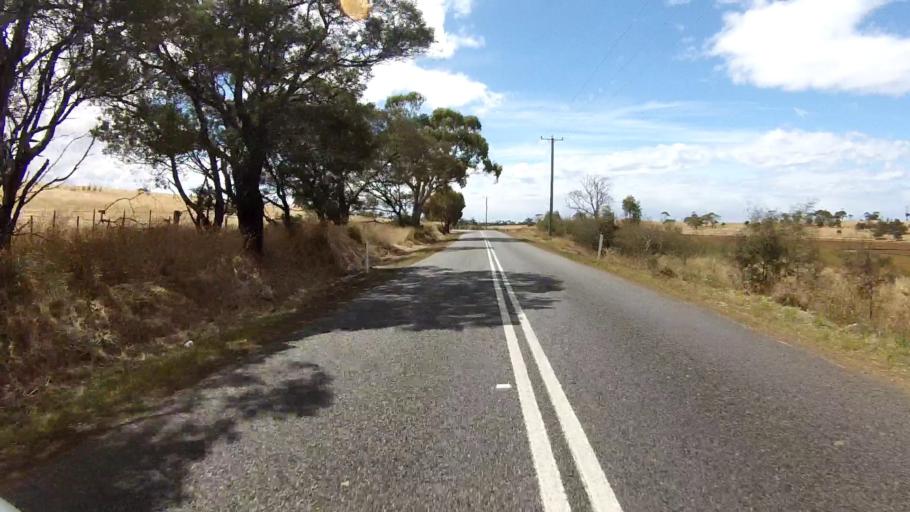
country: AU
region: Tasmania
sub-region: Sorell
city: Sorell
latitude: -42.2784
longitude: 148.0027
